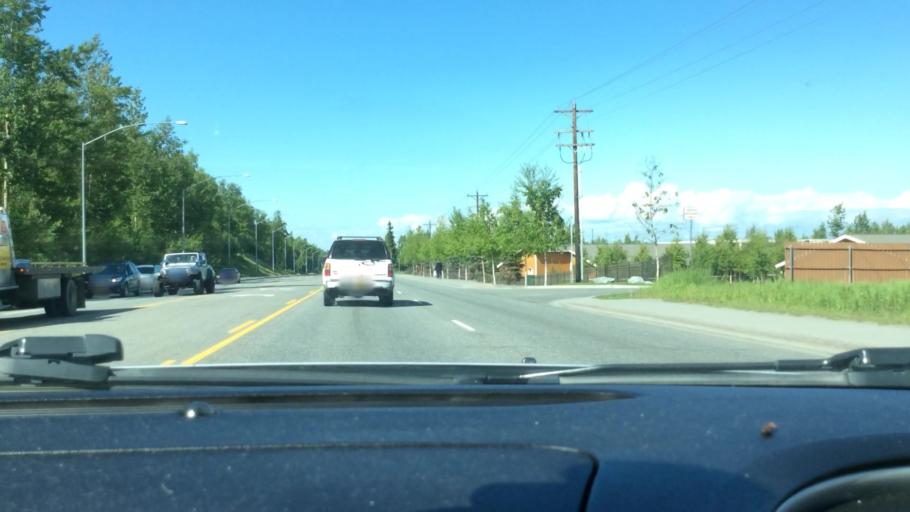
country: US
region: Alaska
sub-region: Anchorage Municipality
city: Anchorage
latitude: 61.2114
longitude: -149.7784
